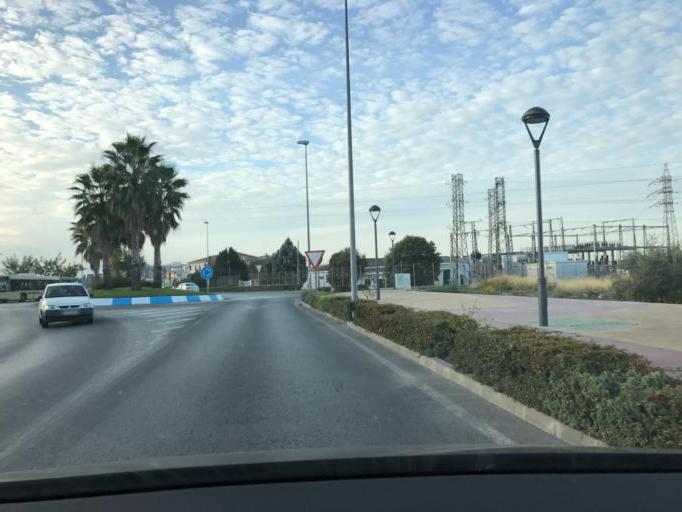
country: ES
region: Andalusia
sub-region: Provincia de Granada
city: Pulianas
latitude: 37.2183
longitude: -3.6097
